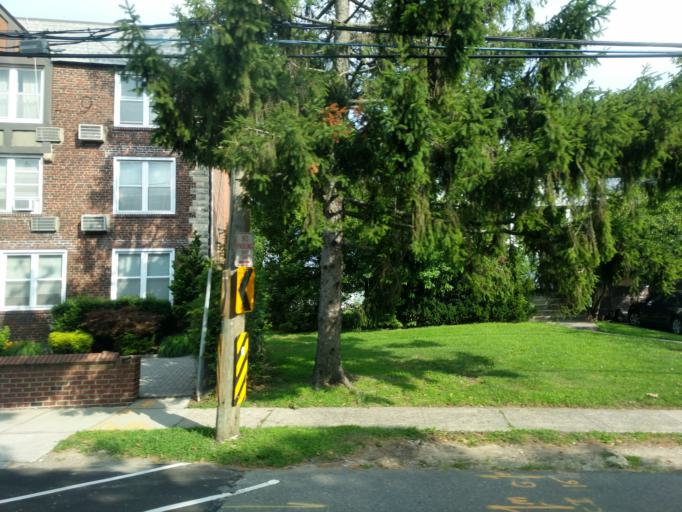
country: US
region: New York
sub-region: Nassau County
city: Woodmere
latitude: 40.6332
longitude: -73.7150
